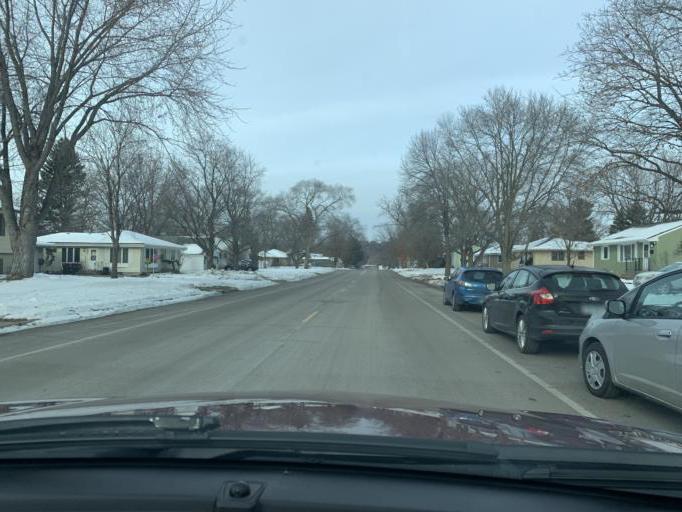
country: US
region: Minnesota
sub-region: Washington County
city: Saint Paul Park
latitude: 44.8393
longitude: -92.9841
